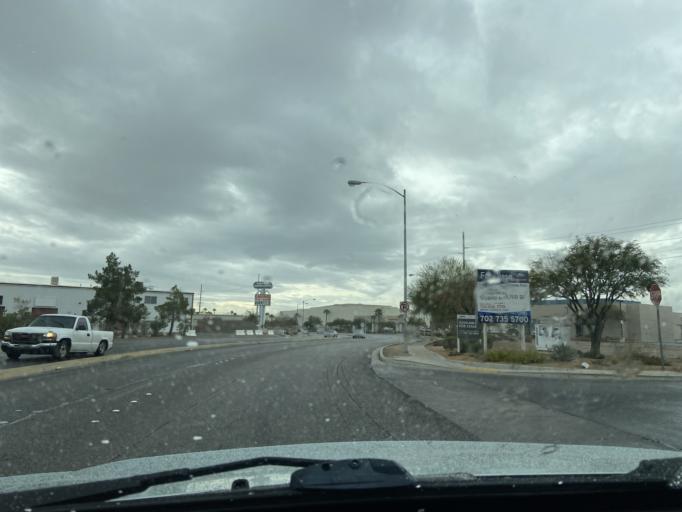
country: US
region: Nevada
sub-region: Clark County
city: Sunrise Manor
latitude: 36.2390
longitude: -115.0976
